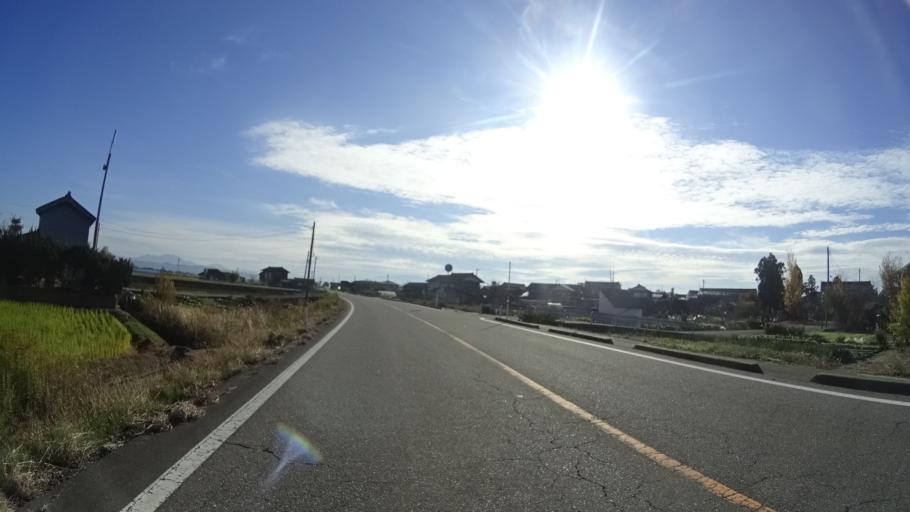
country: JP
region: Niigata
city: Mitsuke
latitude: 37.5760
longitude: 138.8367
